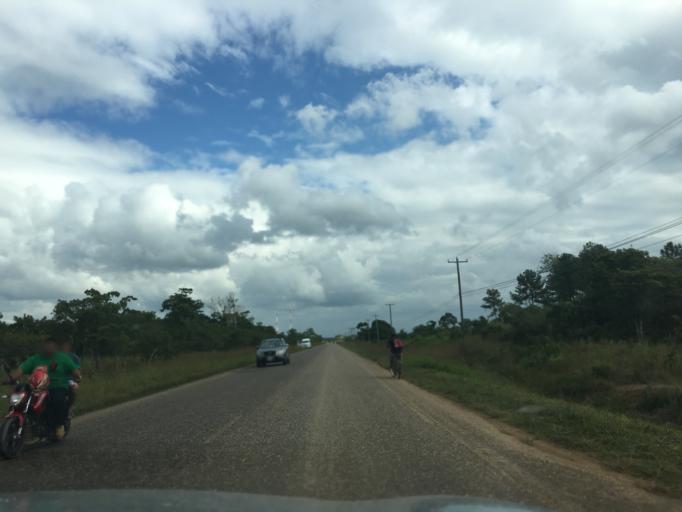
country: BZ
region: Stann Creek
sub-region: Dangriga
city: Dangriga
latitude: 16.8769
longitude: -88.3448
